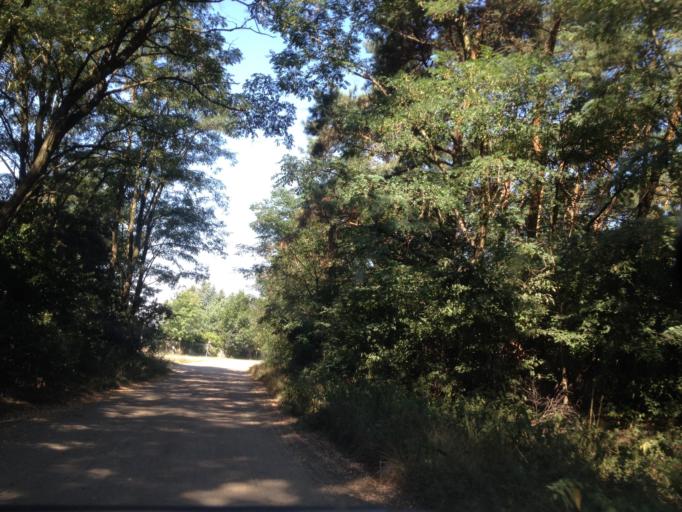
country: PL
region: Greater Poland Voivodeship
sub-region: Powiat sredzki
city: Zaniemysl
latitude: 52.1114
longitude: 17.1193
